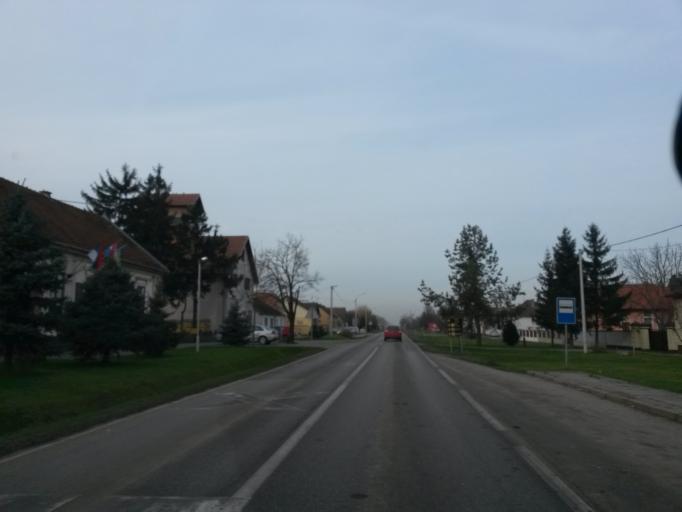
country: HR
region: Vukovarsko-Srijemska
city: Trpinja
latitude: 45.4193
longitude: 18.8996
